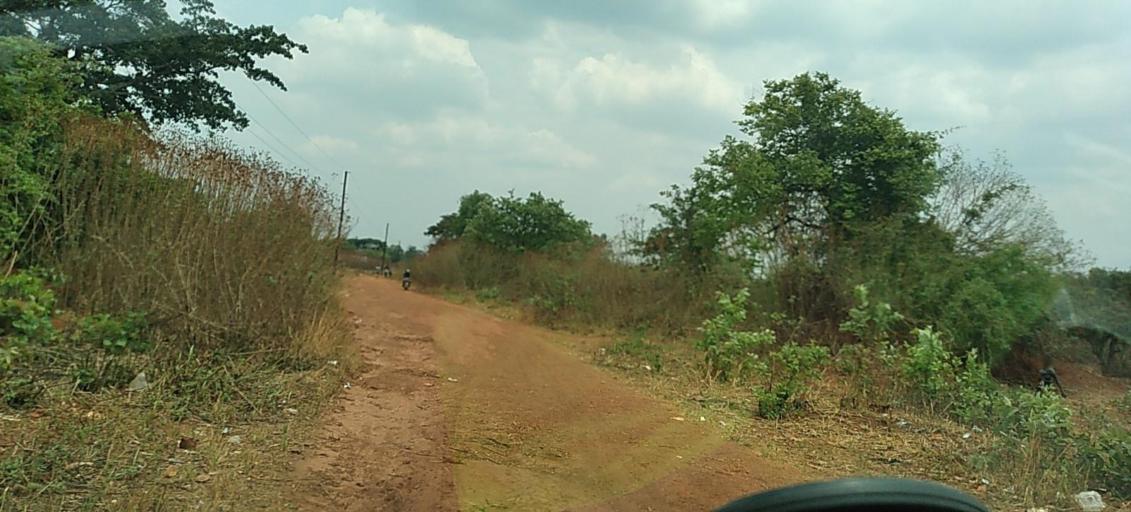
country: ZM
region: North-Western
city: Kansanshi
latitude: -12.0396
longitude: 26.3982
